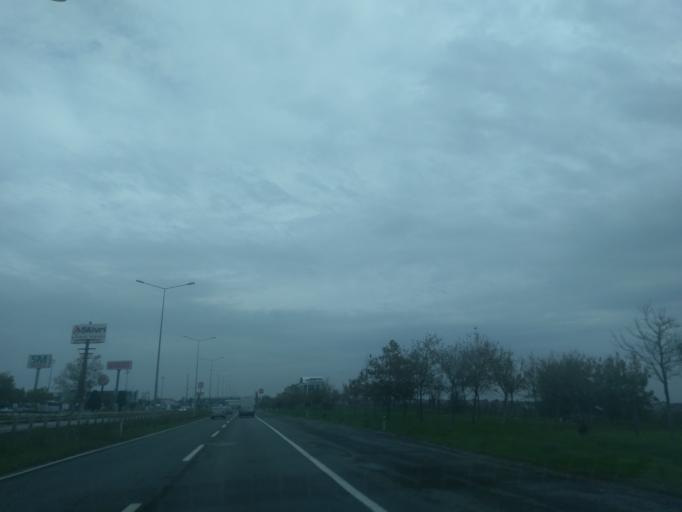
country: TR
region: Istanbul
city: Silivri
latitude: 41.0799
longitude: 28.2011
